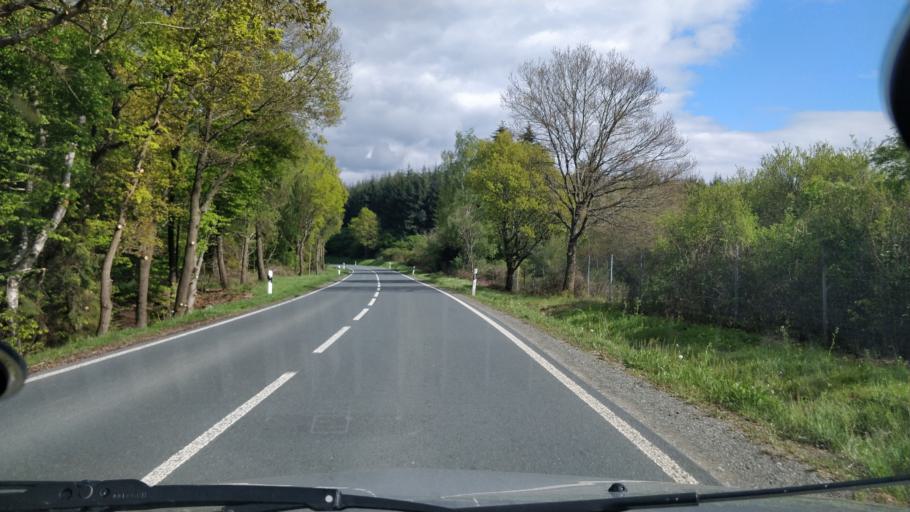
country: DE
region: Hesse
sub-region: Regierungsbezirk Darmstadt
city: Neu-Anspach
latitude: 50.3347
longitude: 8.4858
